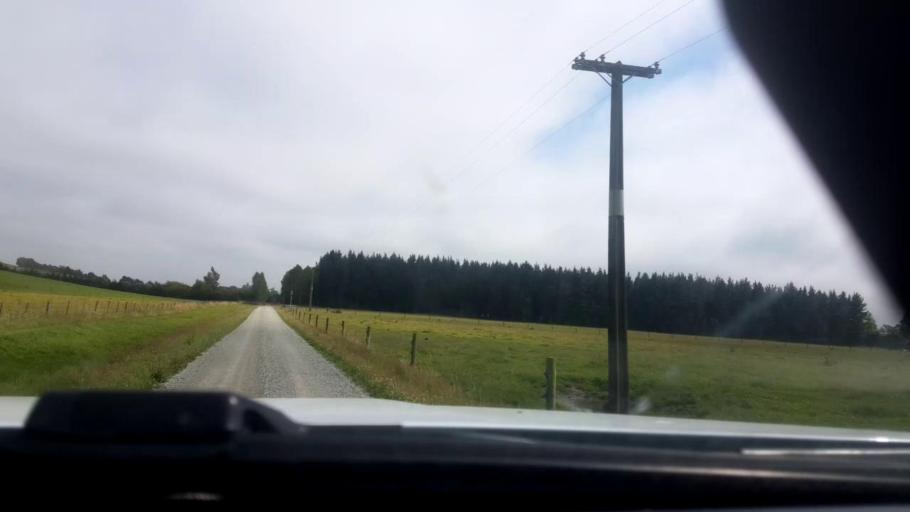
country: NZ
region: Canterbury
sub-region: Timaru District
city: Timaru
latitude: -44.3308
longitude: 171.1991
